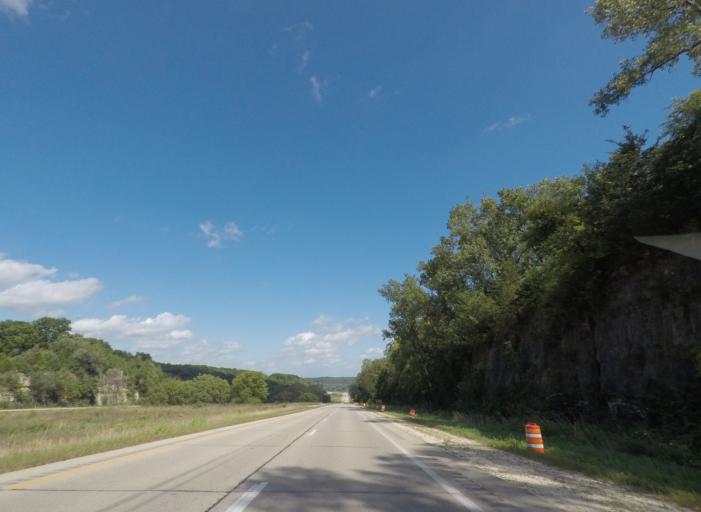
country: US
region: Iowa
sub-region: Dubuque County
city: Dubuque
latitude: 42.4174
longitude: -90.7191
